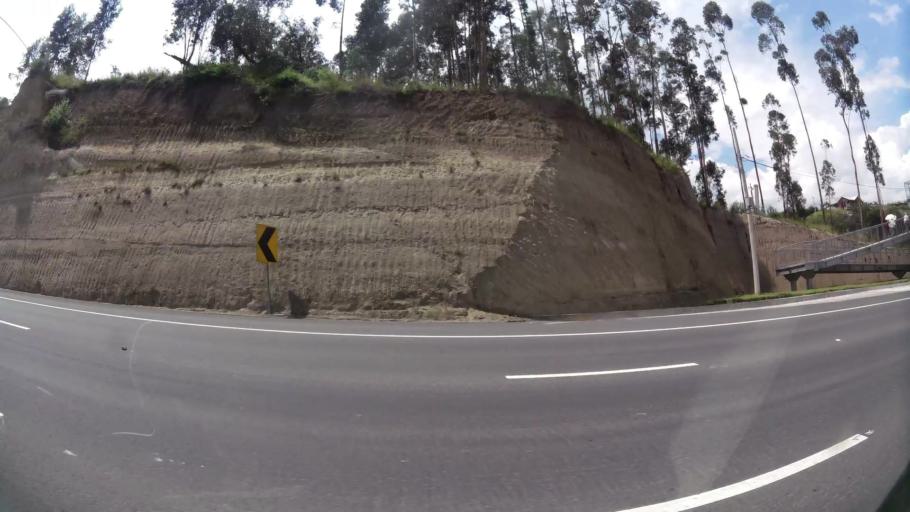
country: EC
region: Pichincha
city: Sangolqui
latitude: -0.2087
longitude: -78.3310
